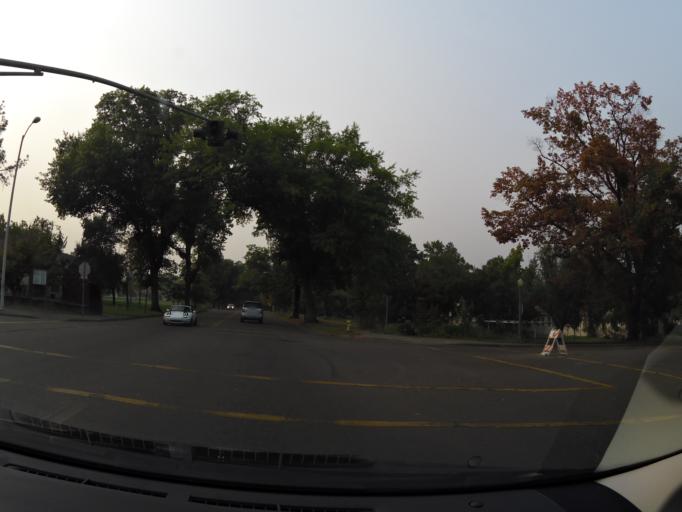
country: US
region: California
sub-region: Sonoma County
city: Eldridge
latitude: 38.3486
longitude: -122.5165
